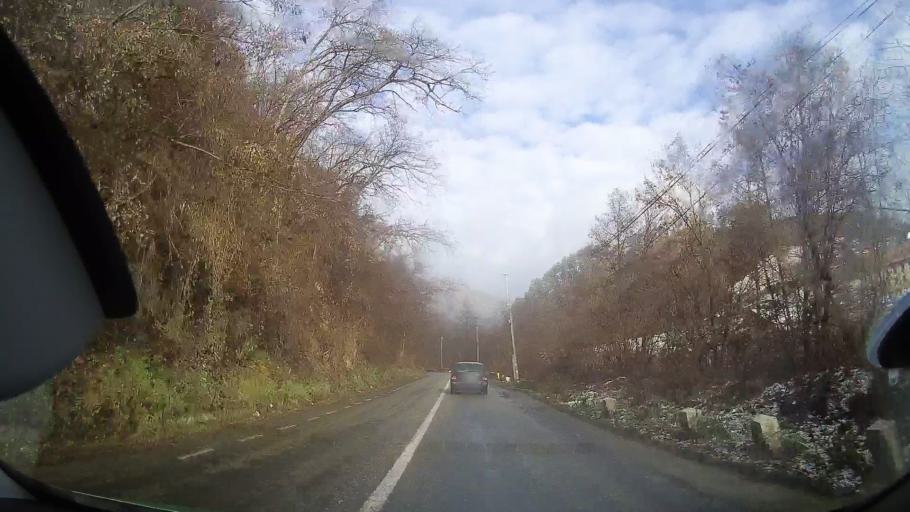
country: RO
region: Alba
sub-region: Oras Baia de Aries
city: Baia de Aries
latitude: 46.3827
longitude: 23.2817
